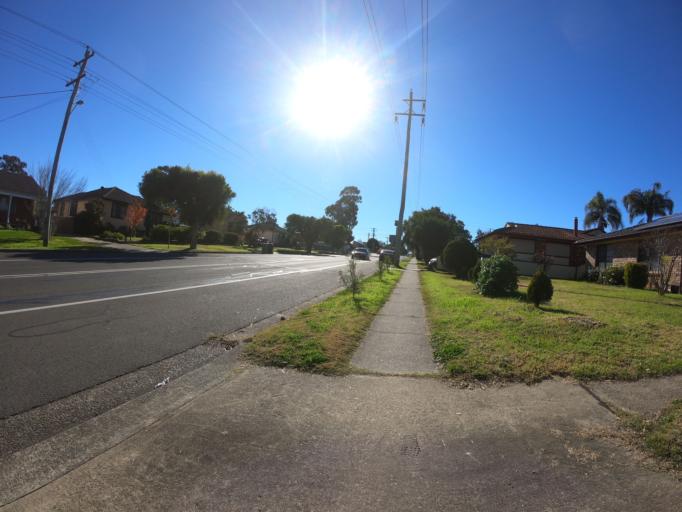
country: AU
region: New South Wales
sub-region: Hawkesbury
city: South Windsor
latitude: -33.6284
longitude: 150.7989
